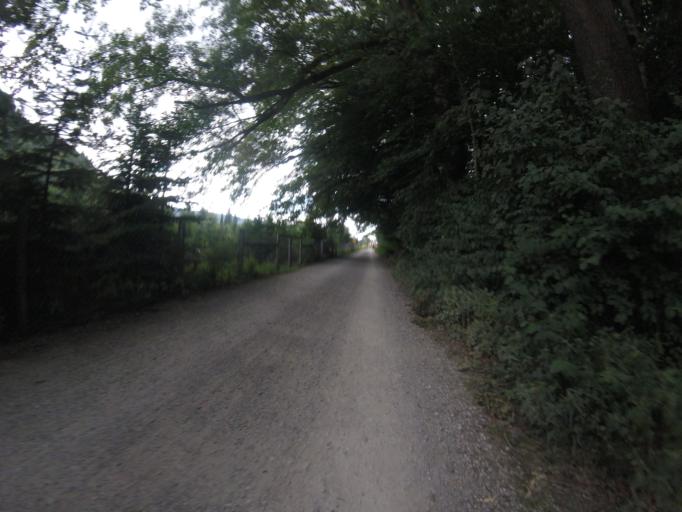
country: CH
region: Bern
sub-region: Bern-Mittelland District
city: Rubigen
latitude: 46.8869
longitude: 7.5298
